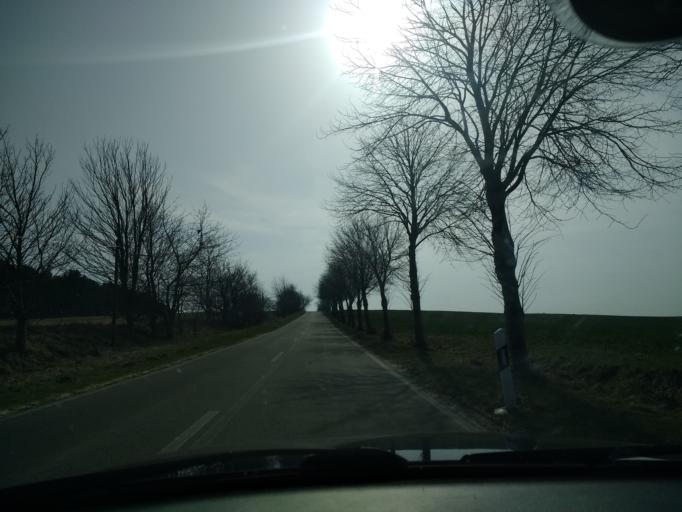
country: DE
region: Mecklenburg-Vorpommern
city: Bergen auf Ruegen
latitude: 54.4419
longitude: 13.4760
